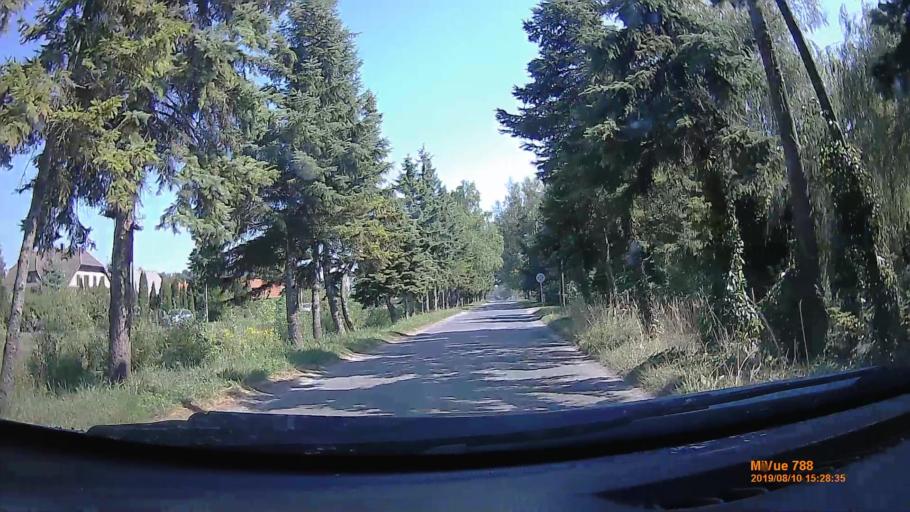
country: HU
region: Somogy
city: Balatonfenyves
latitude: 46.7102
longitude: 17.4784
